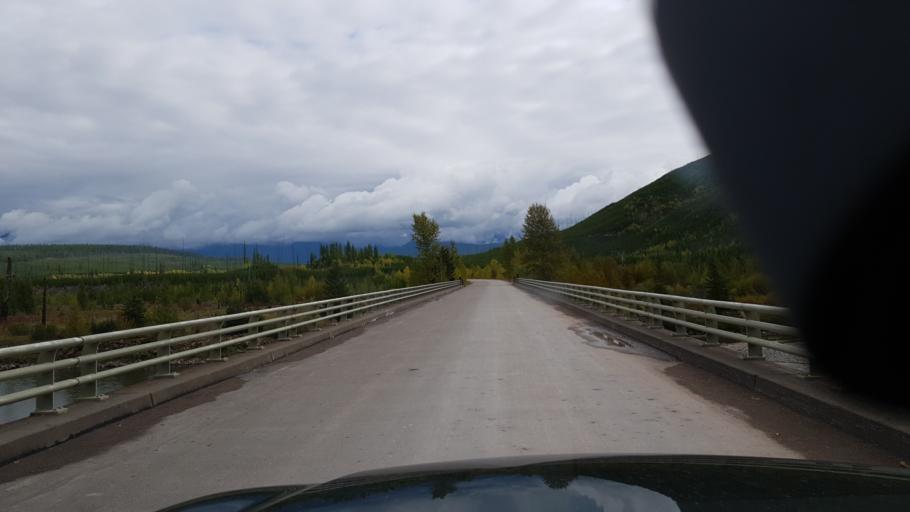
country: US
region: Montana
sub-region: Flathead County
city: Columbia Falls
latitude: 48.6206
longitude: -114.1393
